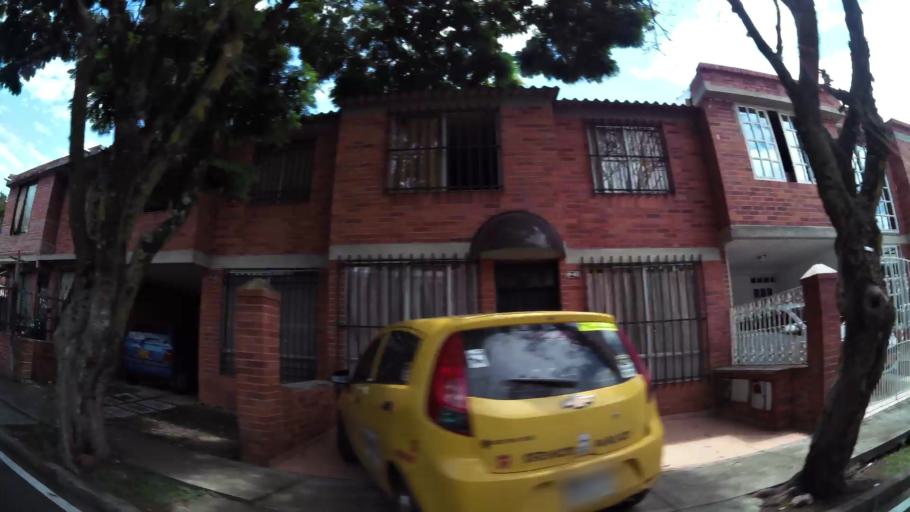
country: CO
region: Valle del Cauca
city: Cali
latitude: 3.3863
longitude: -76.5151
